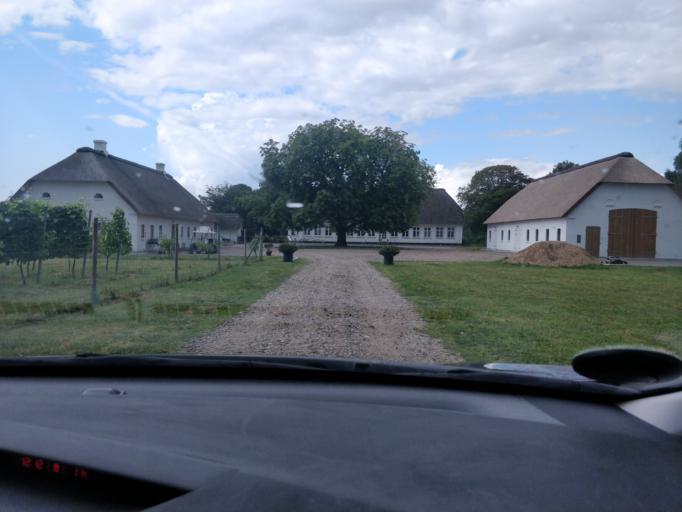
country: DK
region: South Denmark
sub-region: Assens Kommune
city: Assens
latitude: 55.2566
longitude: 9.7405
